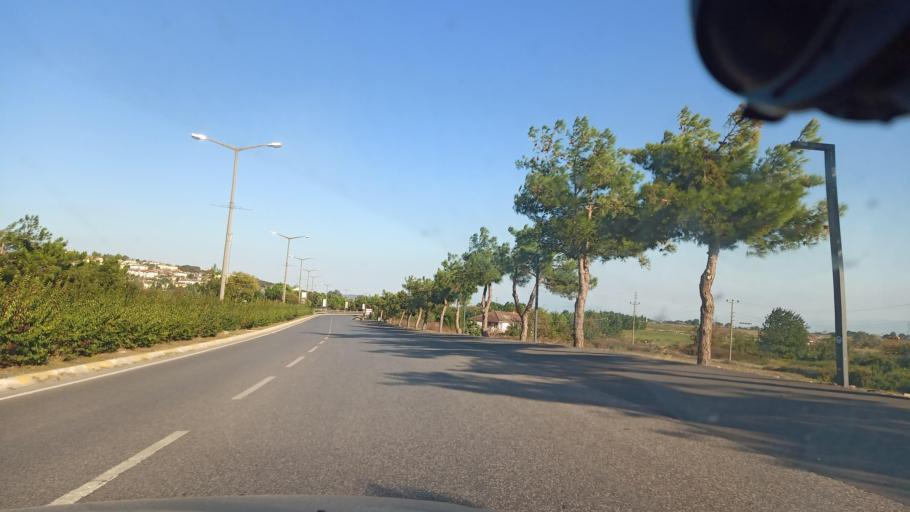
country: TR
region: Sakarya
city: Kazimpasa
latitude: 40.8494
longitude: 30.3196
